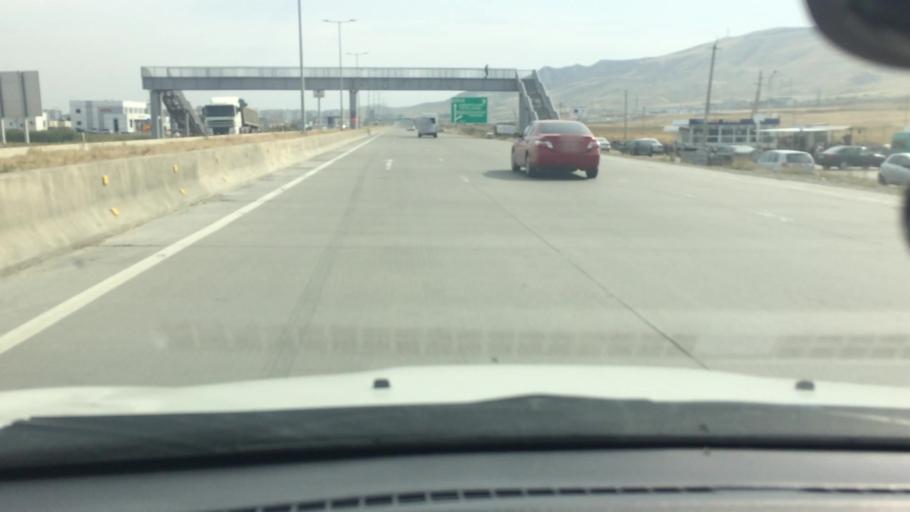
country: GE
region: Kvemo Kartli
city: Rust'avi
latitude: 41.5826
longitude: 44.9519
